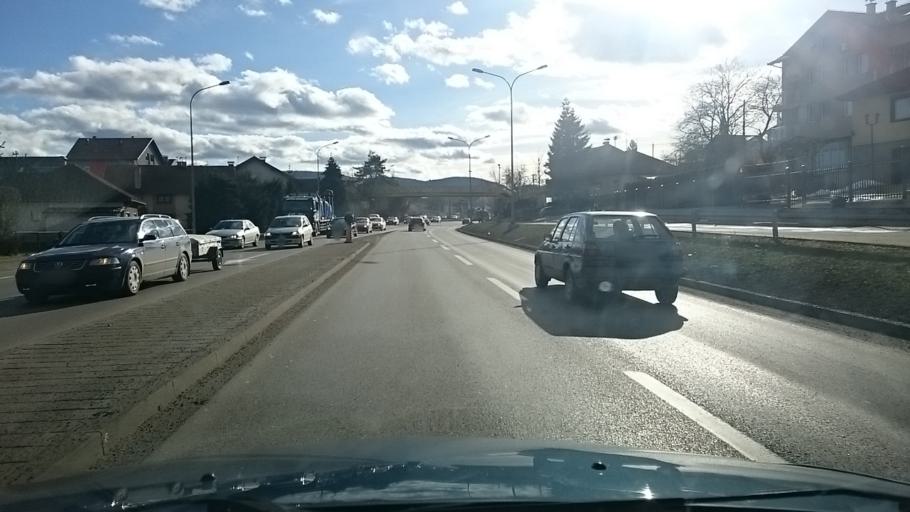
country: BA
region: Republika Srpska
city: Banja Luka
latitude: 44.7896
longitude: 17.1988
